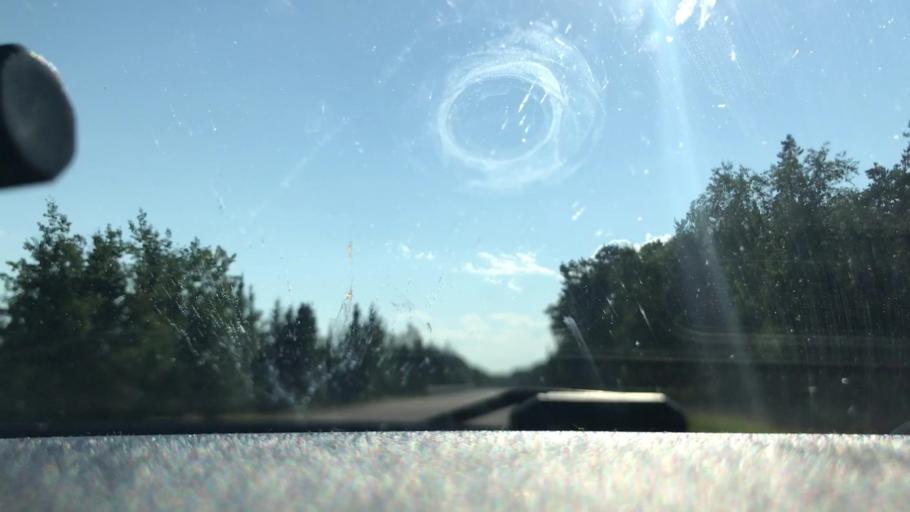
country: US
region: Minnesota
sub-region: Cook County
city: Grand Marais
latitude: 47.8280
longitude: -90.0040
